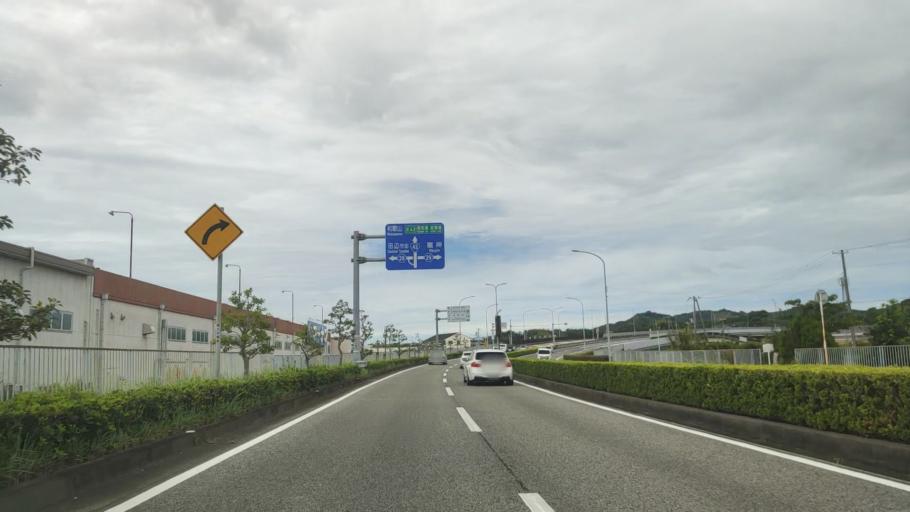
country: JP
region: Wakayama
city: Tanabe
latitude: 33.7408
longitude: 135.3901
